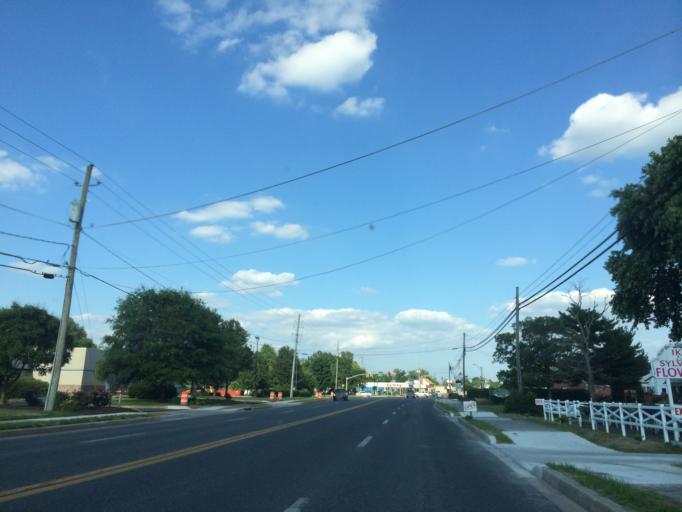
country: US
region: Maryland
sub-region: Wicomico County
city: Salisbury
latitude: 38.3680
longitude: -75.5755
